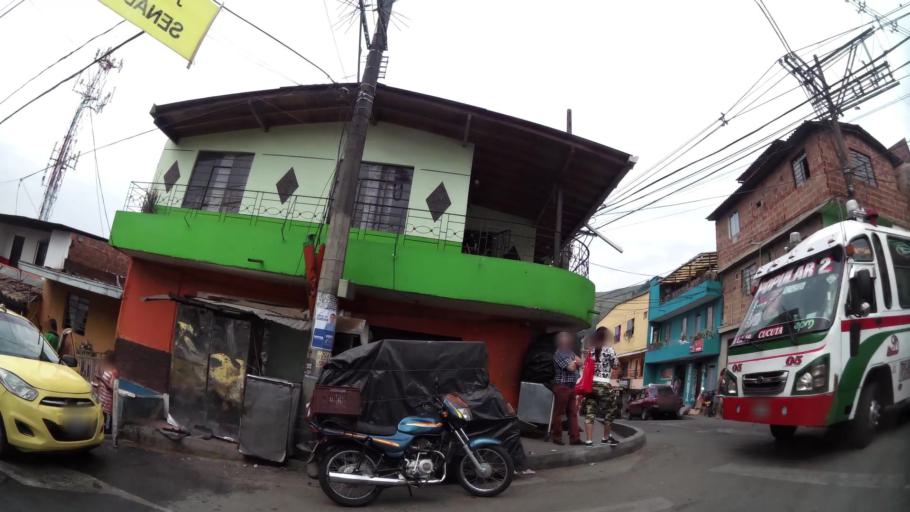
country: CO
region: Antioquia
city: Bello
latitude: 6.3027
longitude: -75.5489
